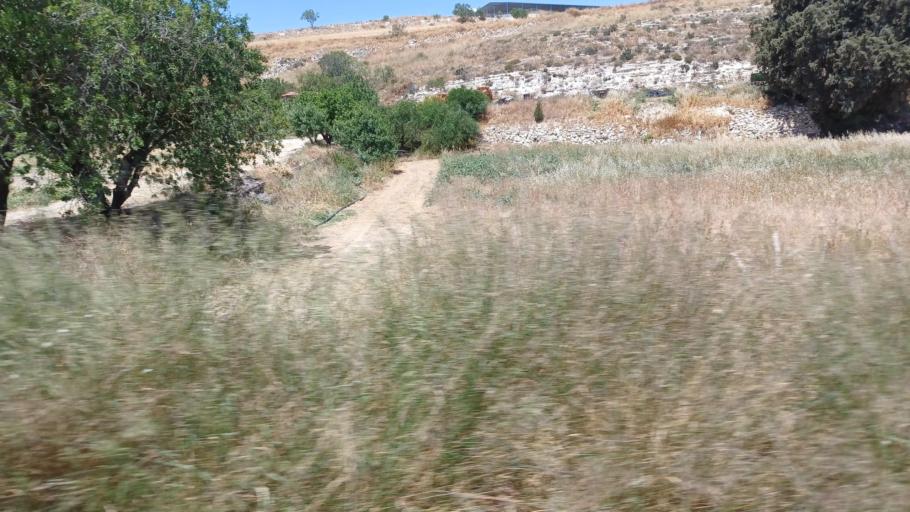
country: CY
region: Larnaka
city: Athienou
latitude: 35.0343
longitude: 33.5418
